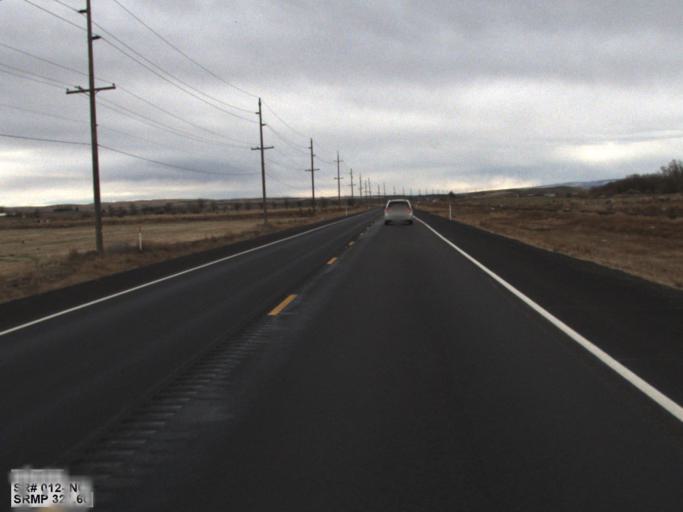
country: US
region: Washington
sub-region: Walla Walla County
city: Garrett
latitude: 46.0456
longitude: -118.6401
